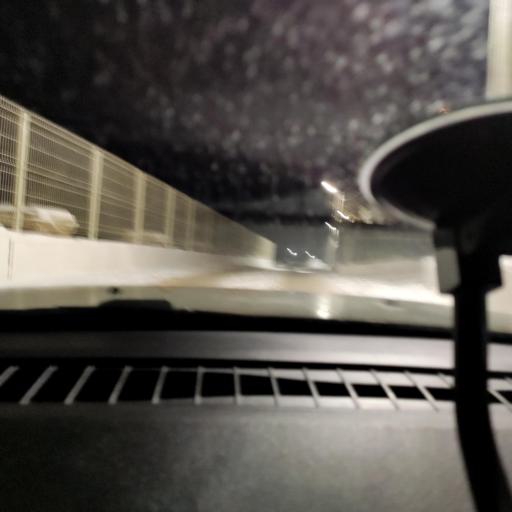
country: RU
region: Samara
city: Samara
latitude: 53.2816
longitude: 50.1891
